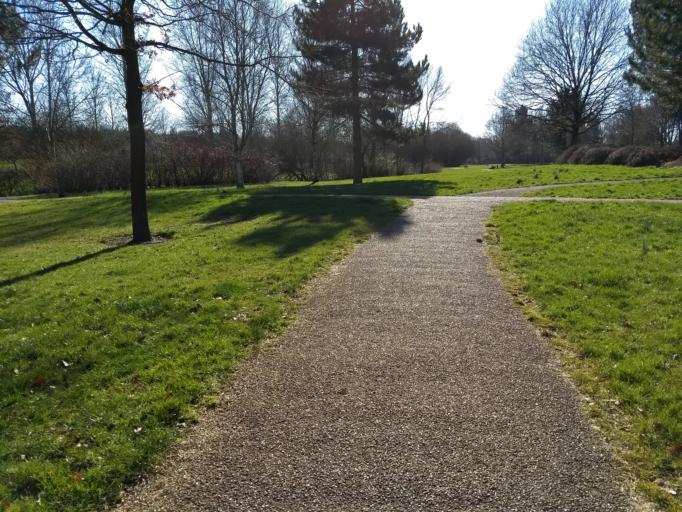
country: GB
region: England
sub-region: Milton Keynes
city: Shenley Church End
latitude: 52.0020
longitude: -0.7752
